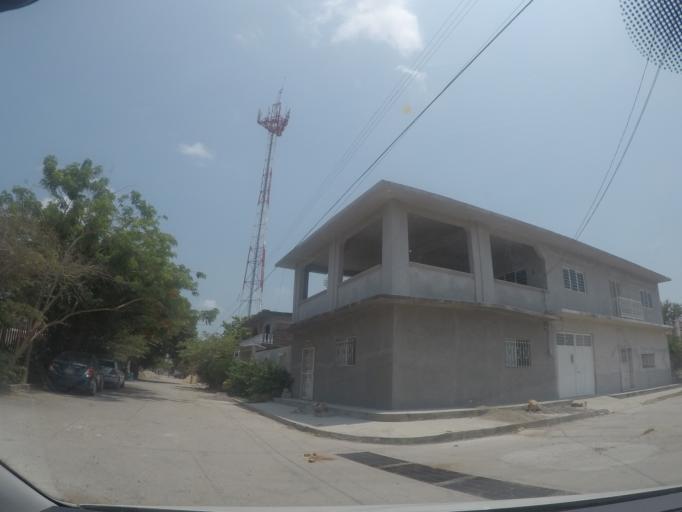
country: MX
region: Oaxaca
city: Asuncion Ixtaltepec
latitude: 16.5053
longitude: -95.0553
